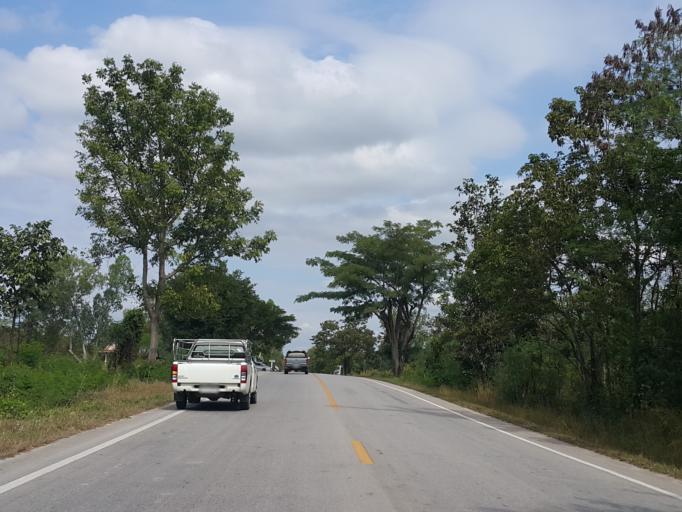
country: TH
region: Lampang
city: Lampang
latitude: 18.3768
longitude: 99.4585
